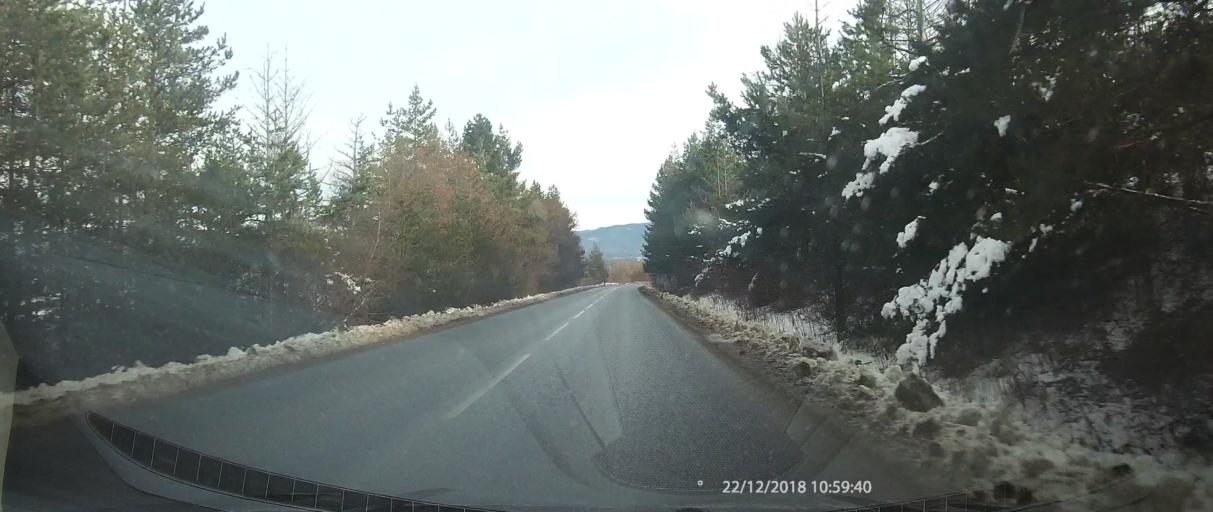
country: MK
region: Kriva Palanka
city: Kriva Palanka
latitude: 42.2279
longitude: 22.4837
